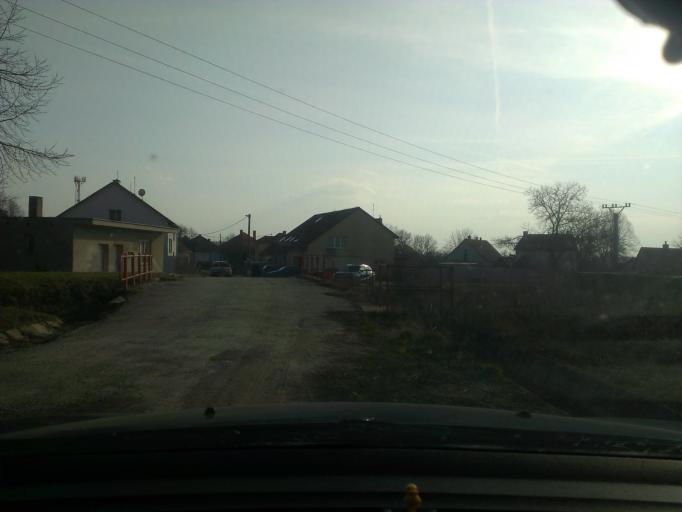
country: SK
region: Trnavsky
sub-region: Okres Trnava
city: Piestany
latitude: 48.6651
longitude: 17.8797
